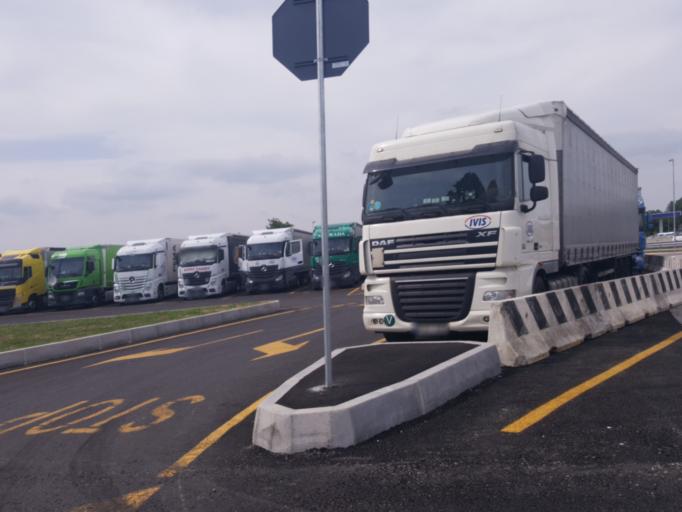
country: IT
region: Lombardy
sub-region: Citta metropolitana di Milano
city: Passirana
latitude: 45.5589
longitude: 9.0385
